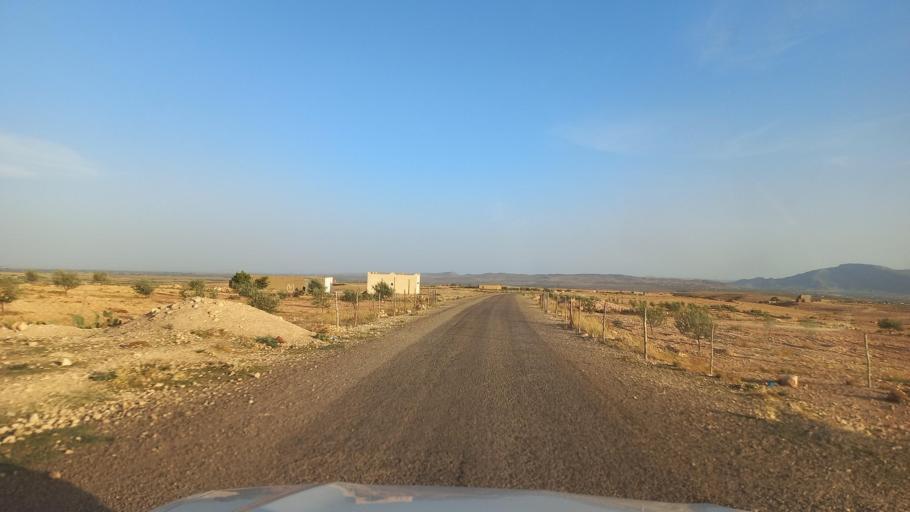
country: TN
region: Al Qasrayn
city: Kasserine
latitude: 35.2757
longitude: 8.9121
